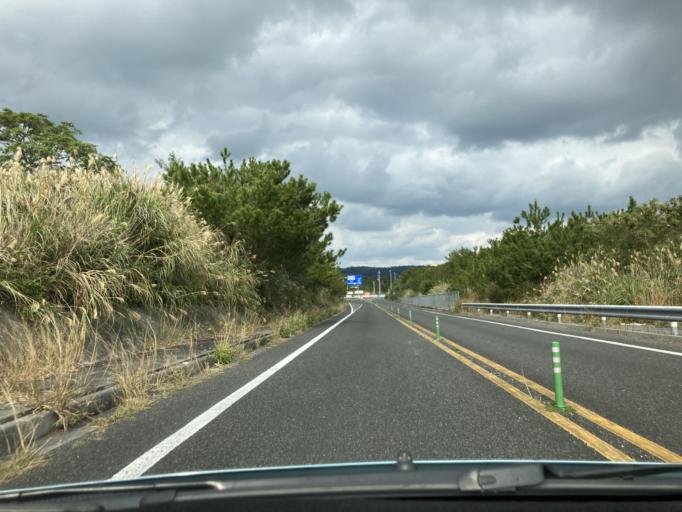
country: JP
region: Okinawa
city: Nago
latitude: 26.6059
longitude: 127.9988
